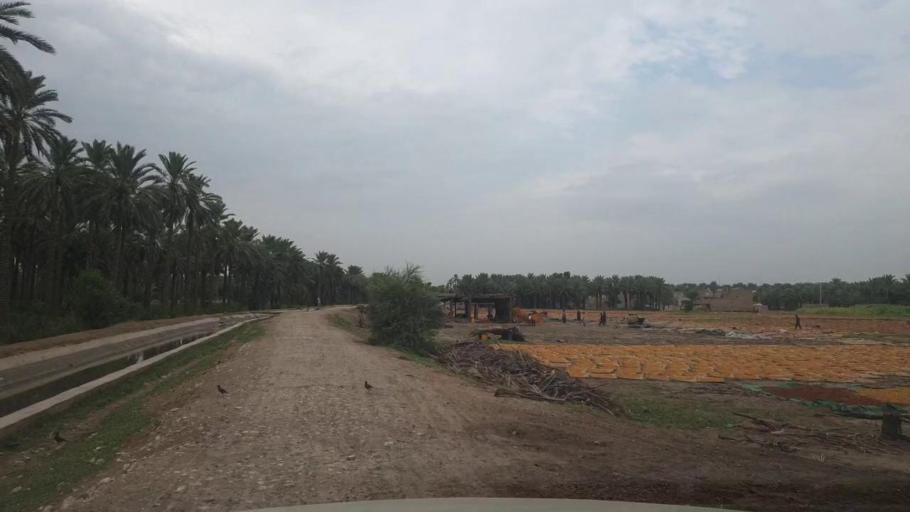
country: PK
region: Sindh
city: Sukkur
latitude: 27.6266
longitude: 68.8204
